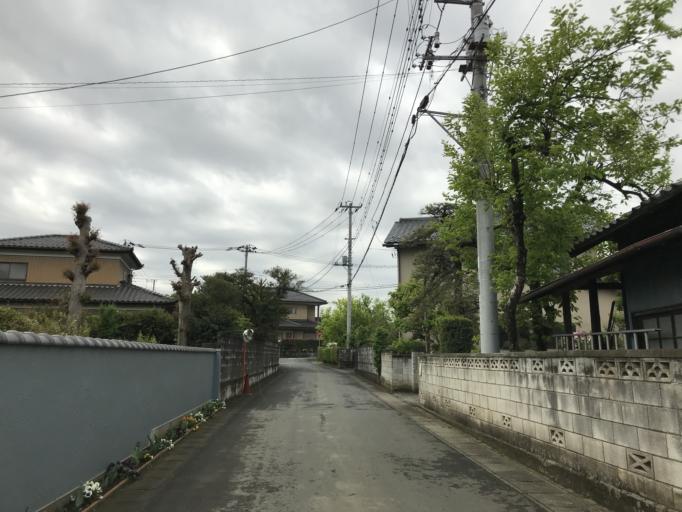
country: JP
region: Ibaraki
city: Moriya
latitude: 35.9318
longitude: 139.9854
